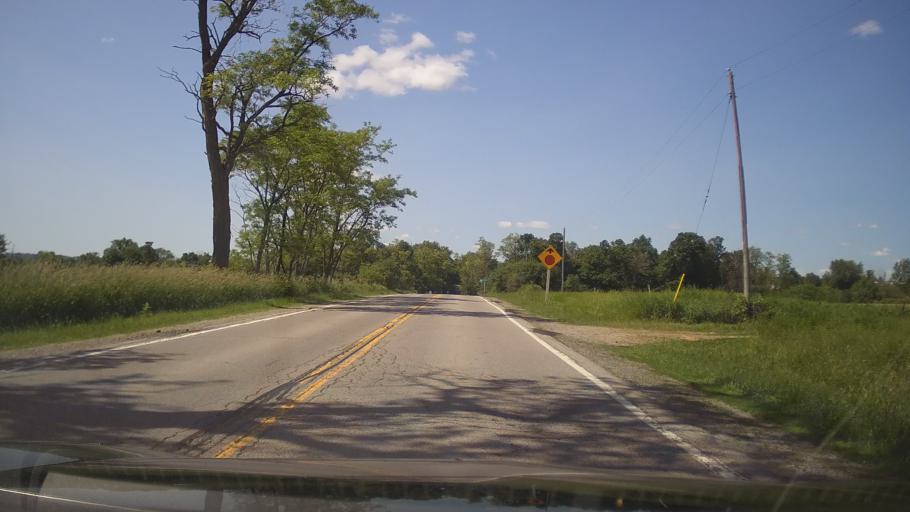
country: CA
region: Ontario
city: Oshawa
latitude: 43.9907
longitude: -78.8612
